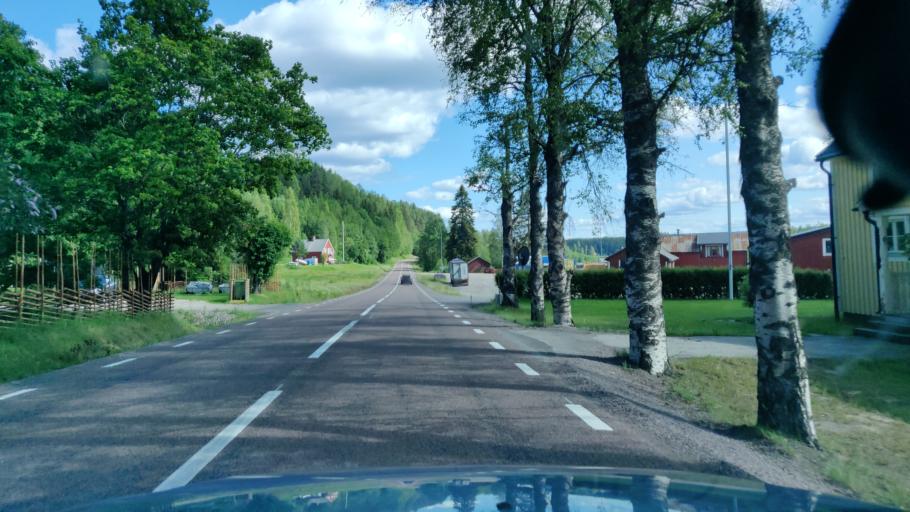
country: SE
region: Vaermland
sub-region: Torsby Kommun
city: Torsby
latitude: 60.6277
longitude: 13.0252
